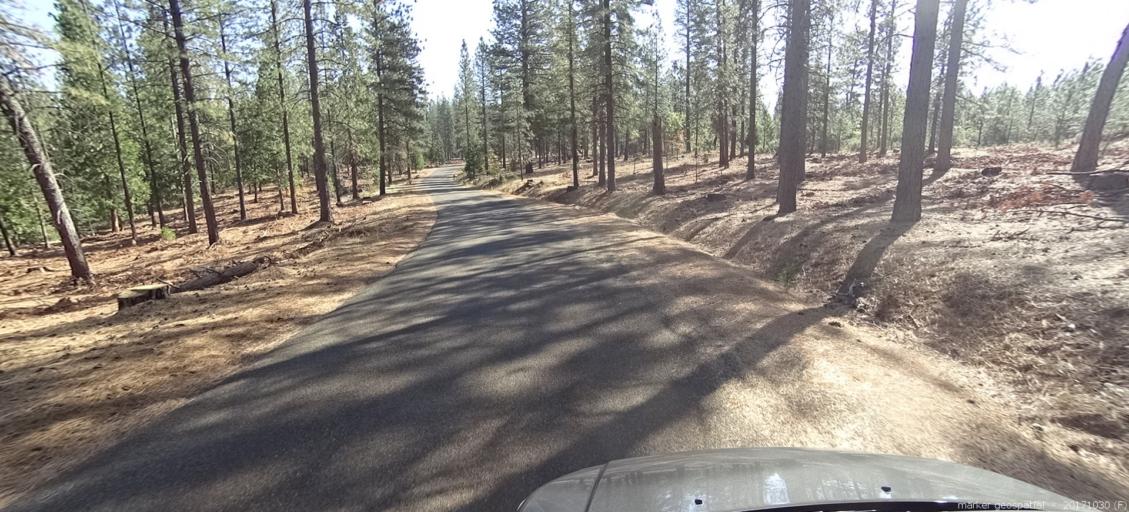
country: US
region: California
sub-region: Shasta County
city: Shingletown
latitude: 40.6183
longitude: -121.8894
